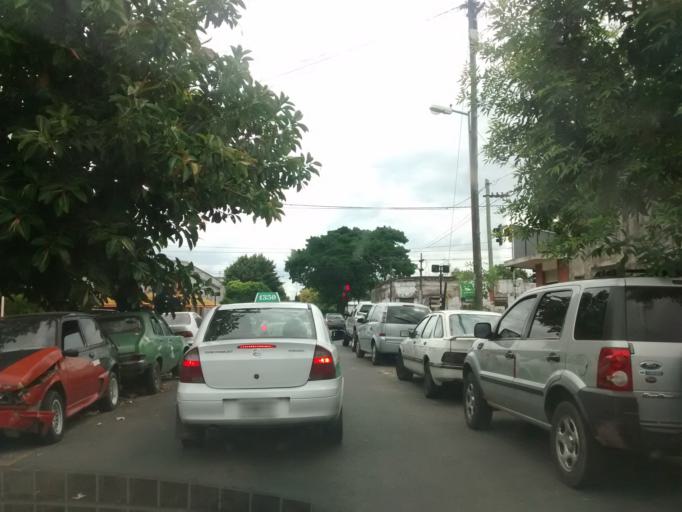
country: AR
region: Buenos Aires
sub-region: Partido de La Plata
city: La Plata
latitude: -34.9325
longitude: -57.9253
